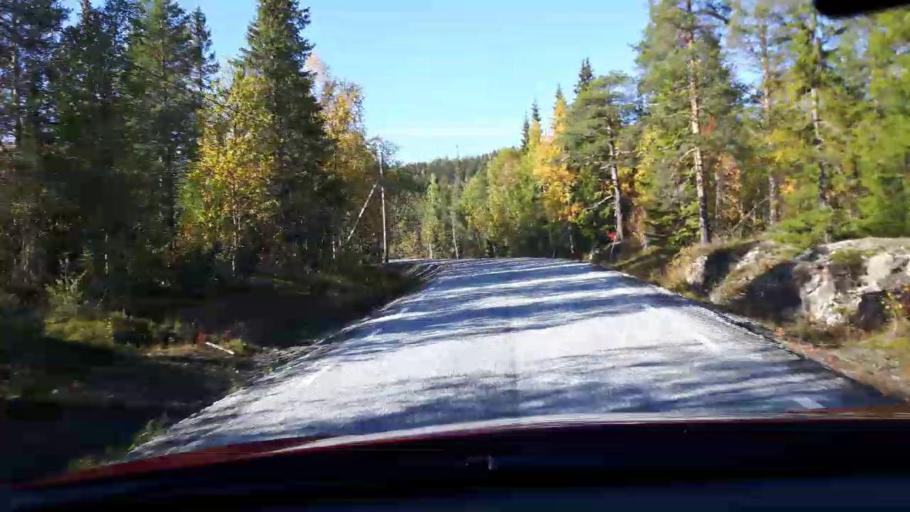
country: NO
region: Nord-Trondelag
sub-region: Royrvik
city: Royrvik
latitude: 64.8188
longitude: 14.2301
